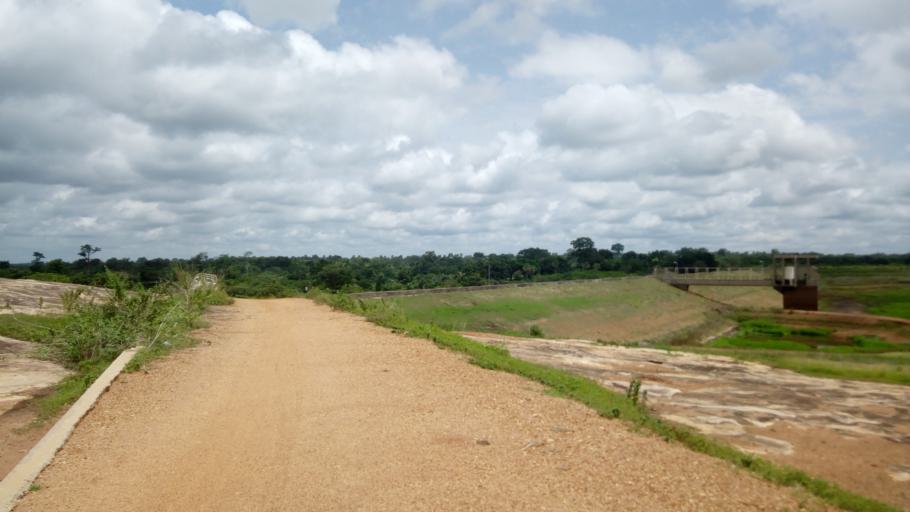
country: CI
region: Vallee du Bandama
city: Botro
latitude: 7.7105
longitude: -5.2248
